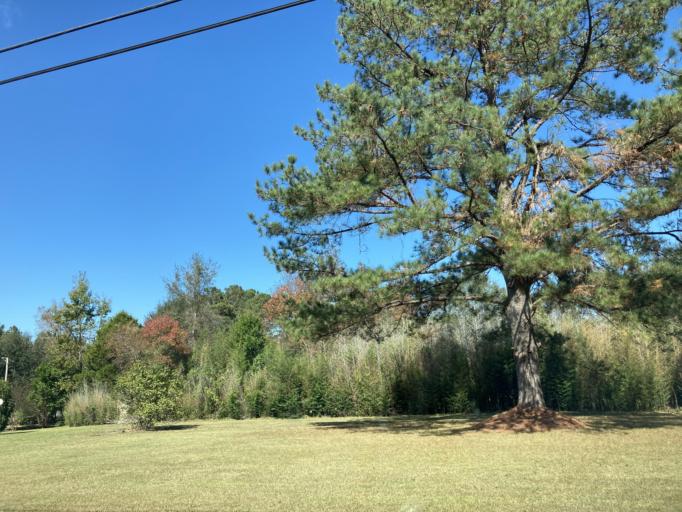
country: US
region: Mississippi
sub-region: Lamar County
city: West Hattiesburg
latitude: 31.2620
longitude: -89.4210
